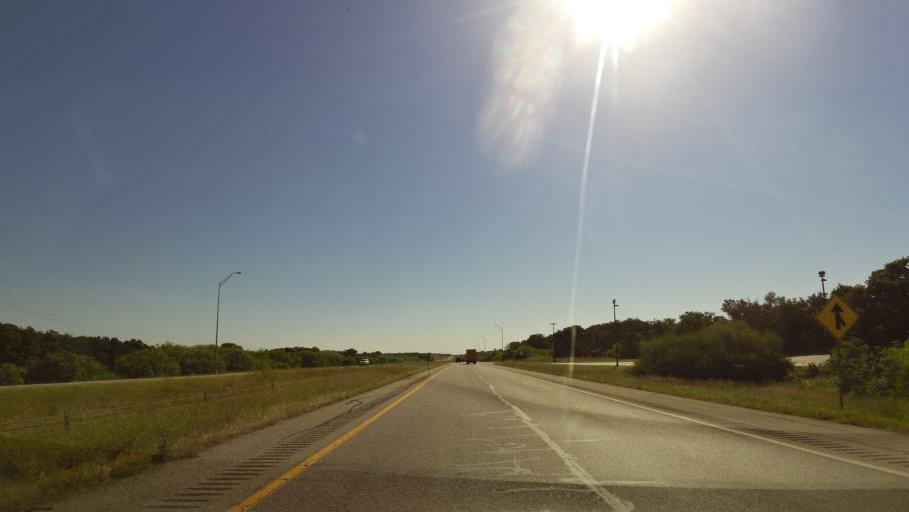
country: US
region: Texas
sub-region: Caldwell County
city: Luling
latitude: 29.6161
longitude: -97.8007
